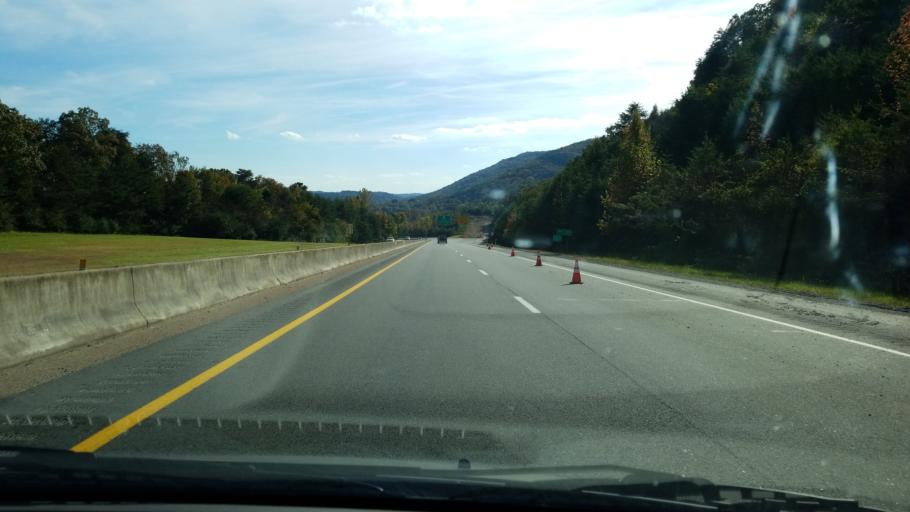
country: US
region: Tennessee
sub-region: Hamilton County
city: Soddy-Daisy
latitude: 35.3113
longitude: -85.1631
